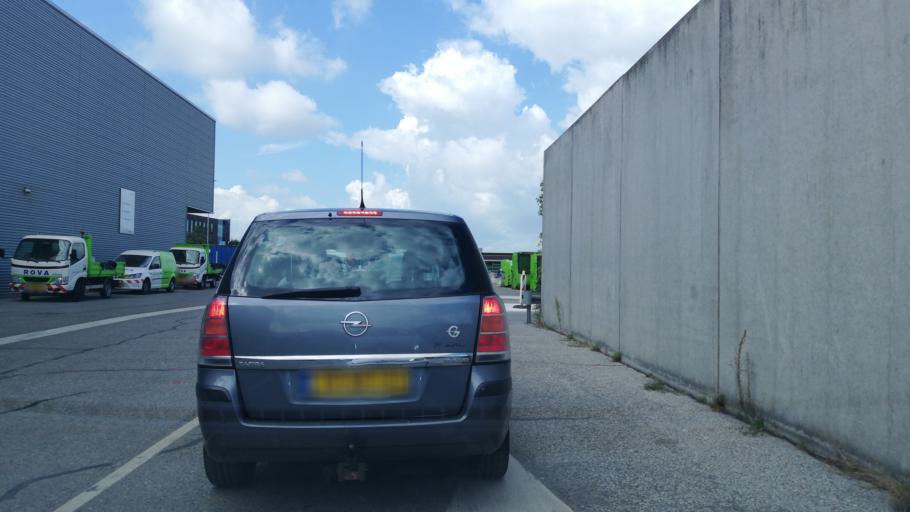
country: NL
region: Overijssel
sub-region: Gemeente Dalfsen
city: Dalfsen
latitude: 52.5303
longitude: 6.1797
